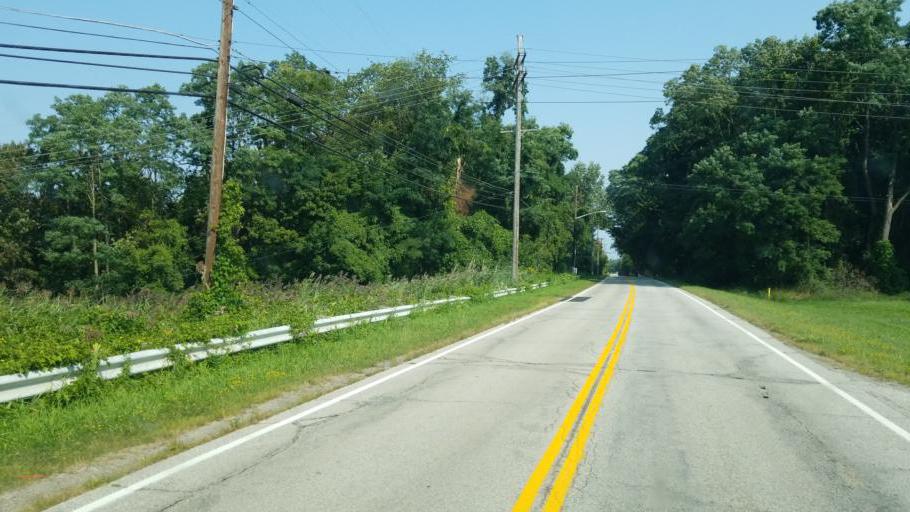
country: US
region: Ohio
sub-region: Lake County
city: Painesville
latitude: 41.7424
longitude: -81.2276
